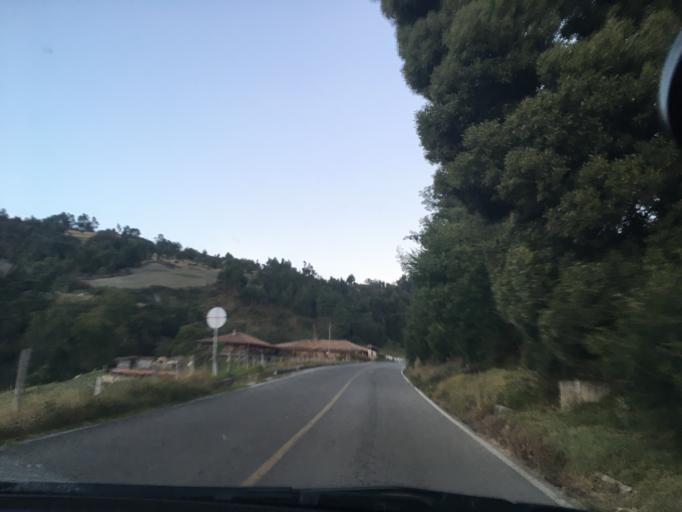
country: CO
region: Boyaca
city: Aquitania
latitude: 5.6095
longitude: -72.9079
